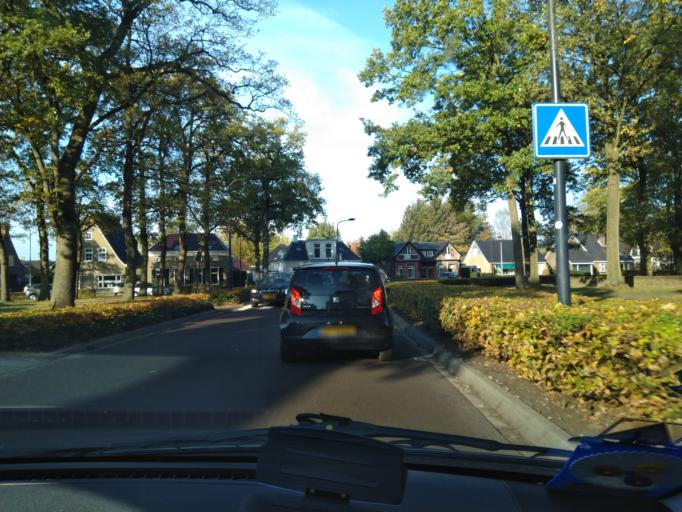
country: NL
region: Drenthe
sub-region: Gemeente Tynaarlo
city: Zuidlaren
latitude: 53.0958
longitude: 6.6869
